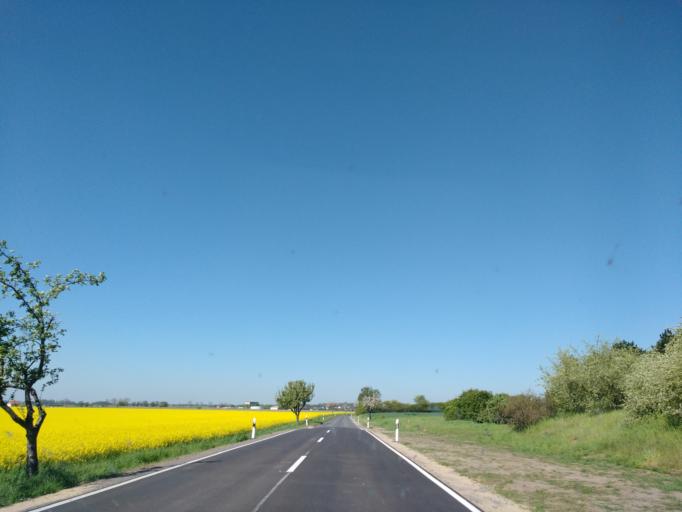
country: DE
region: Saxony-Anhalt
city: Niemberg
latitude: 51.5488
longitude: 12.0770
